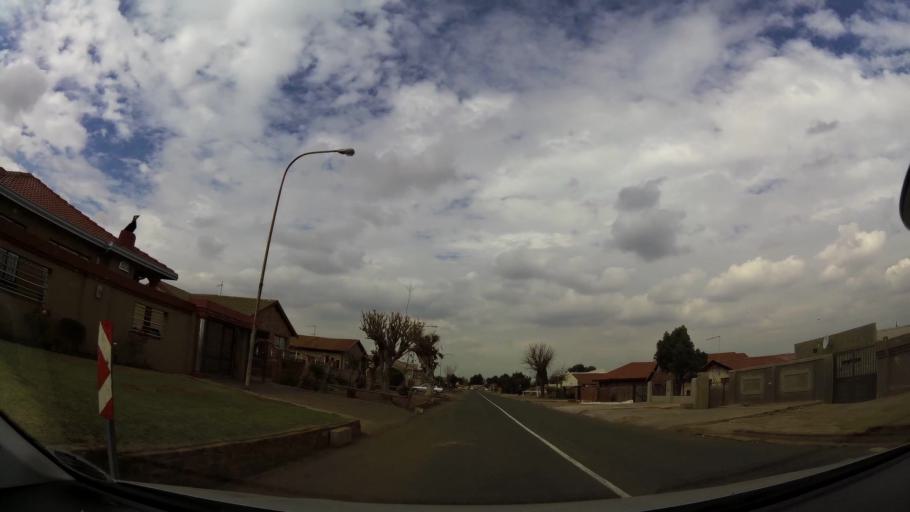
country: ZA
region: Gauteng
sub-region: City of Johannesburg Metropolitan Municipality
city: Soweto
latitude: -26.2771
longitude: 27.8493
